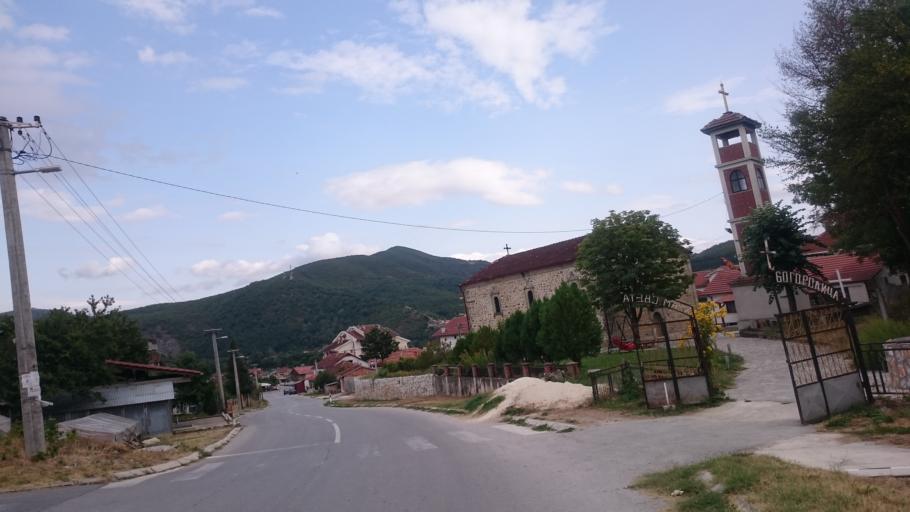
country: MK
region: Makedonski Brod
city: Makedonski Brod
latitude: 41.5140
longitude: 21.2136
